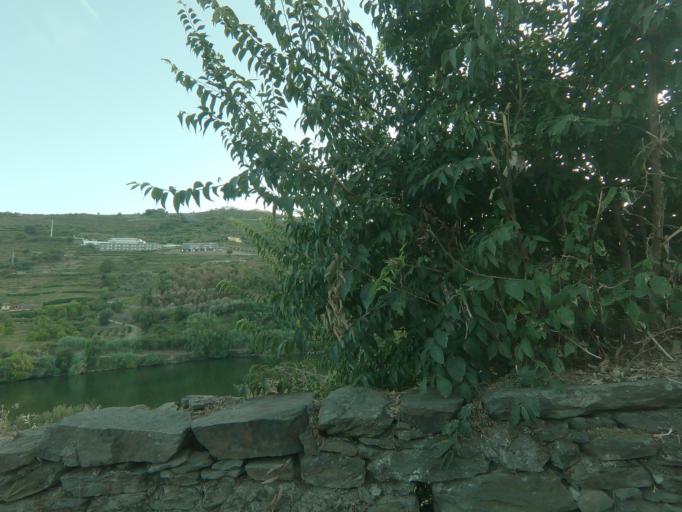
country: PT
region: Vila Real
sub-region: Peso da Regua
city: Godim
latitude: 41.1488
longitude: -7.8200
